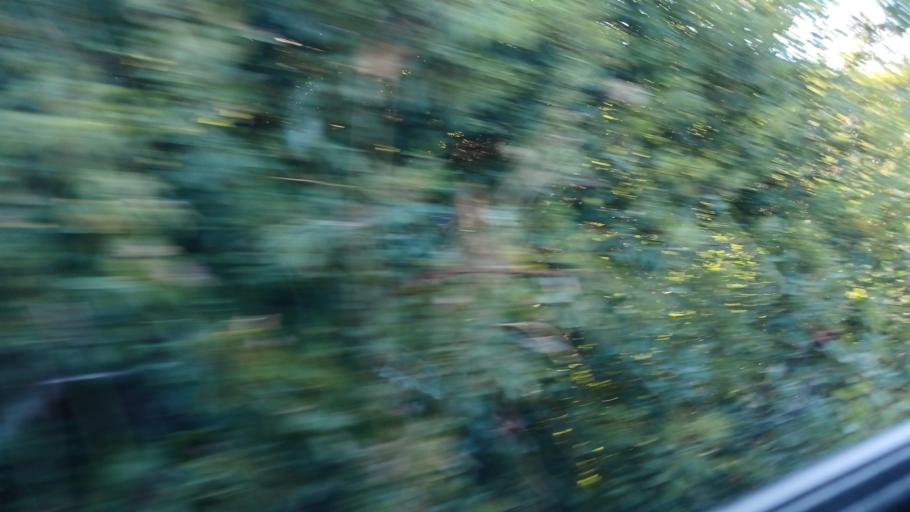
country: CY
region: Pafos
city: Mesogi
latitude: 34.8819
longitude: 32.5242
